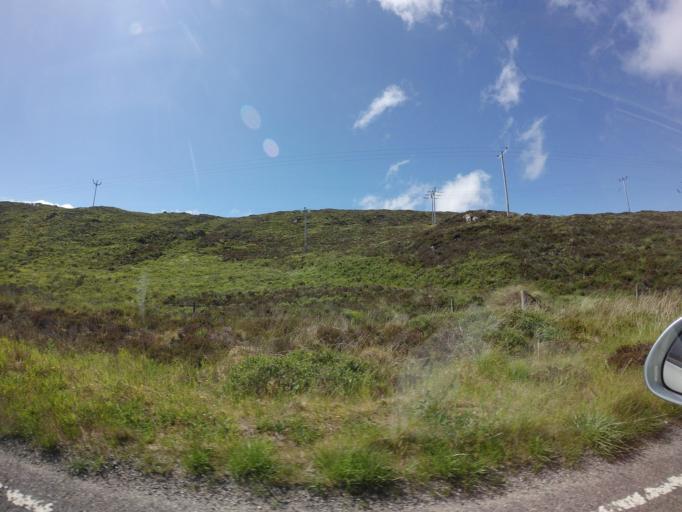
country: GB
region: Scotland
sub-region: Eilean Siar
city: Stornoway
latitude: 58.1398
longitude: -6.5092
